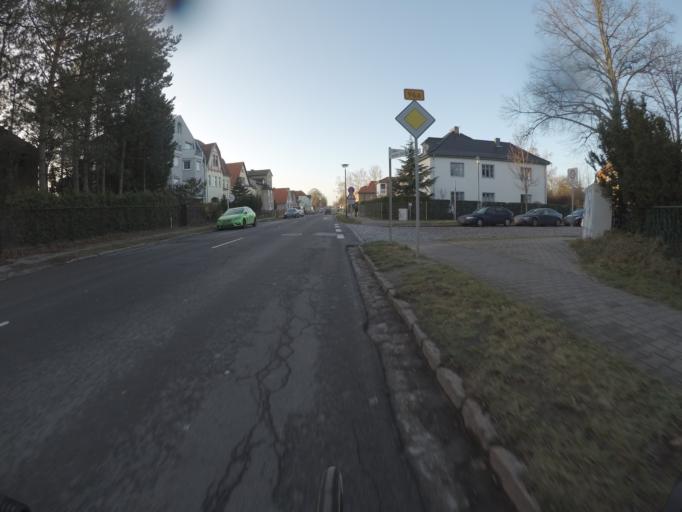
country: DE
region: Brandenburg
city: Birkenwerder
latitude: 52.6860
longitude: 13.2929
